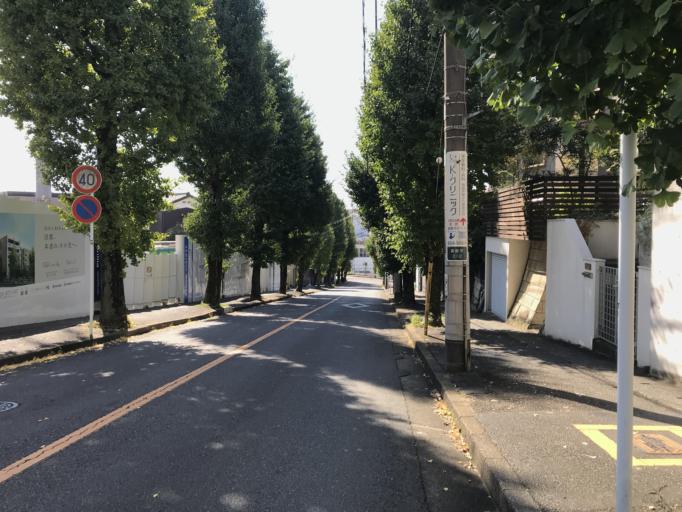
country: JP
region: Tokyo
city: Chofugaoka
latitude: 35.5863
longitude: 139.5847
